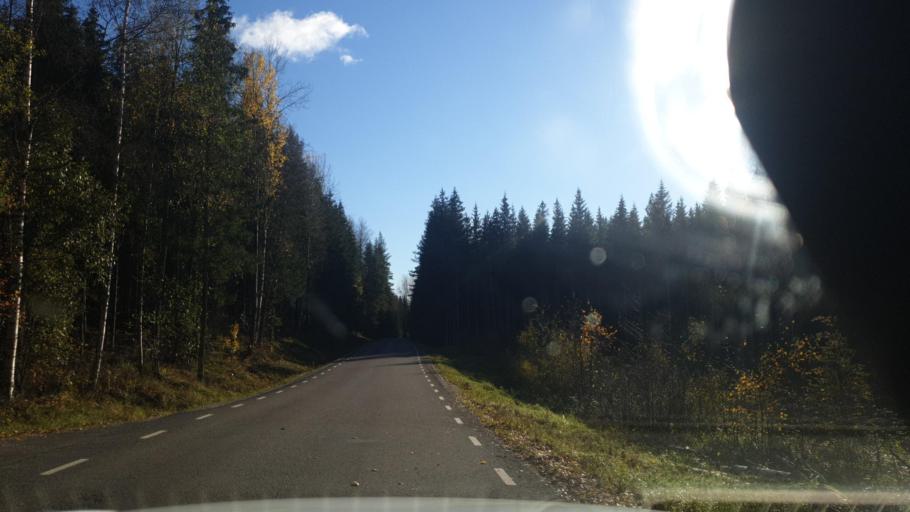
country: SE
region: Vaermland
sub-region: Arvika Kommun
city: Arvika
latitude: 59.6519
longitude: 12.8083
